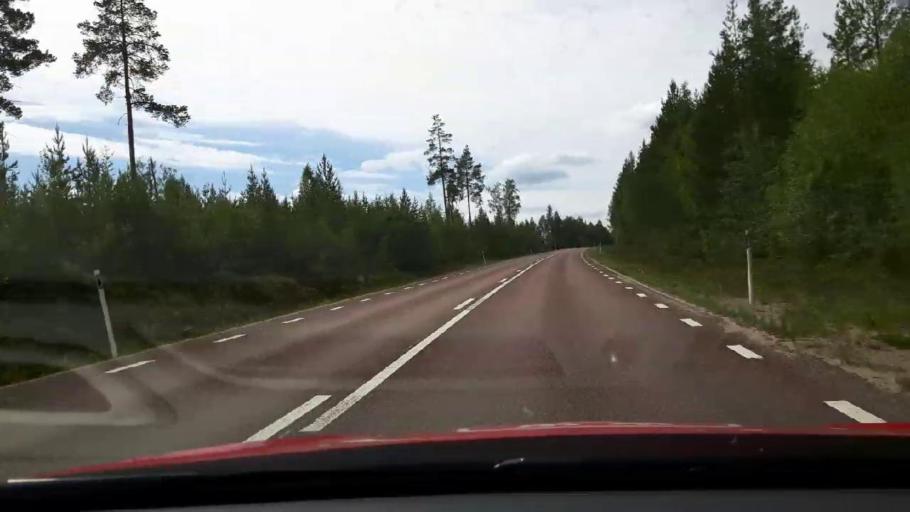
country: SE
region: Jaemtland
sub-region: Harjedalens Kommun
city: Sveg
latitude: 62.0502
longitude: 14.8938
